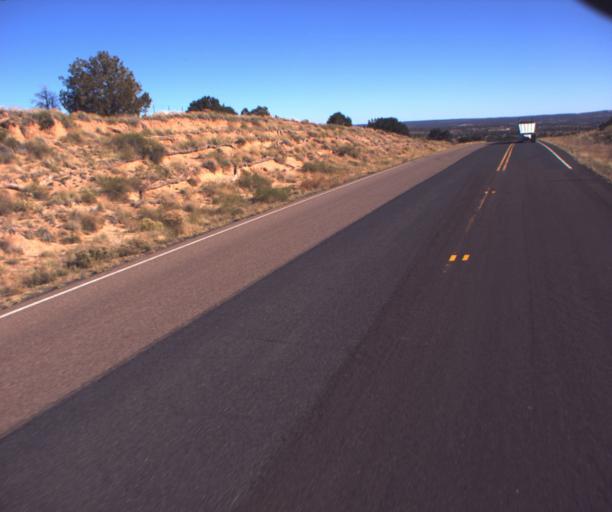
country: US
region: Arizona
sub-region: Apache County
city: Ganado
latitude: 35.4332
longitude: -109.5214
